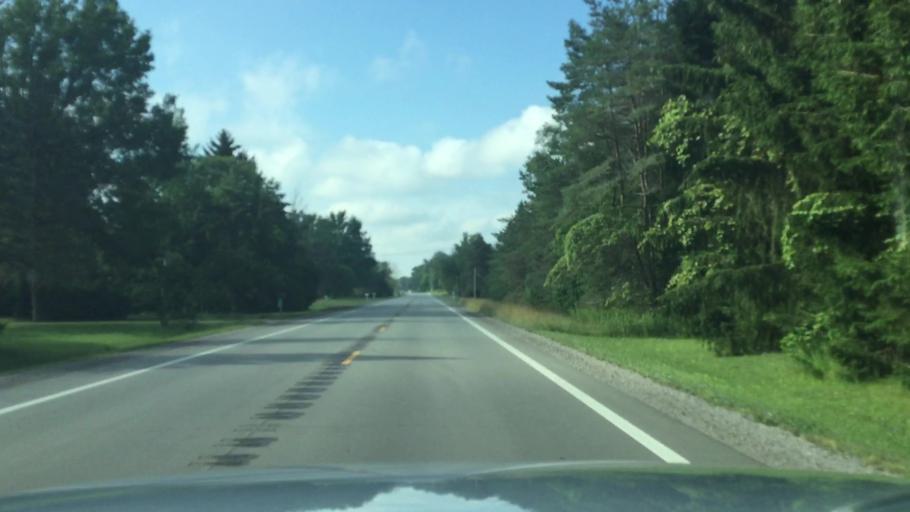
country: US
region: Michigan
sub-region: Genesee County
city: Clio
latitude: 43.2260
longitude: -83.7352
